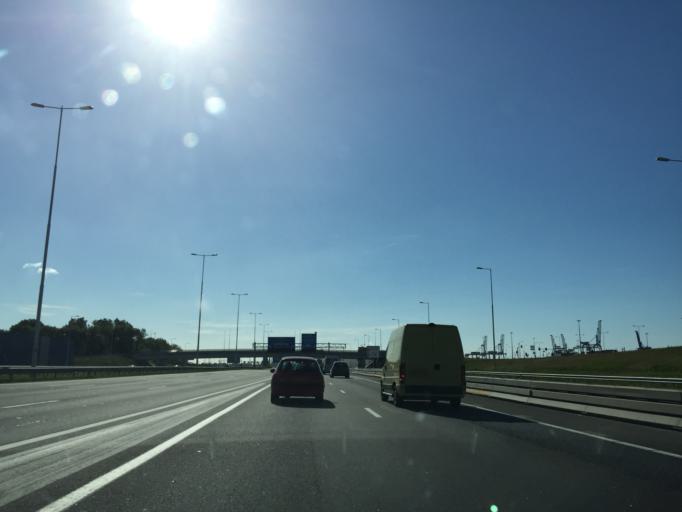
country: NL
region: South Holland
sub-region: Gemeente Albrandswaard
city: Rhoon
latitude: 51.8730
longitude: 4.4163
